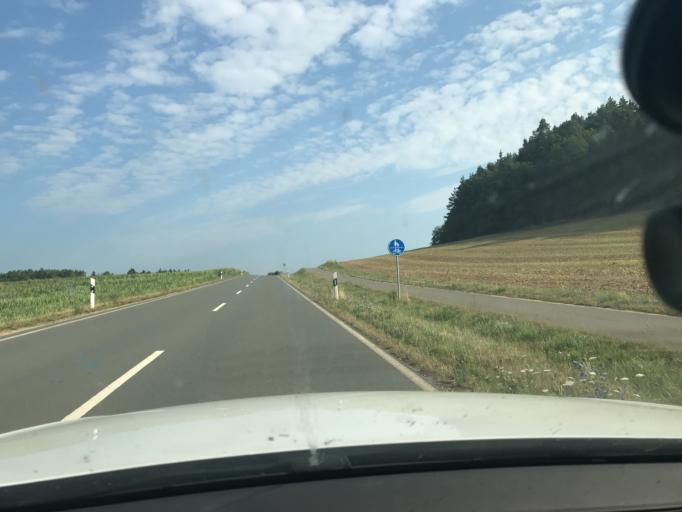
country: DE
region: Bavaria
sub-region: Upper Palatinate
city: Auerbach
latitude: 49.7157
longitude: 11.6189
